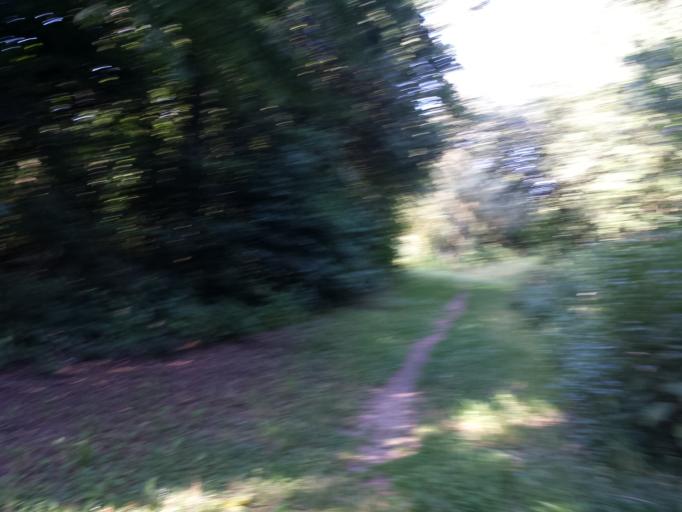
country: DE
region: Lower Saxony
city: Stuhr
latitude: 53.0729
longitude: 8.7638
